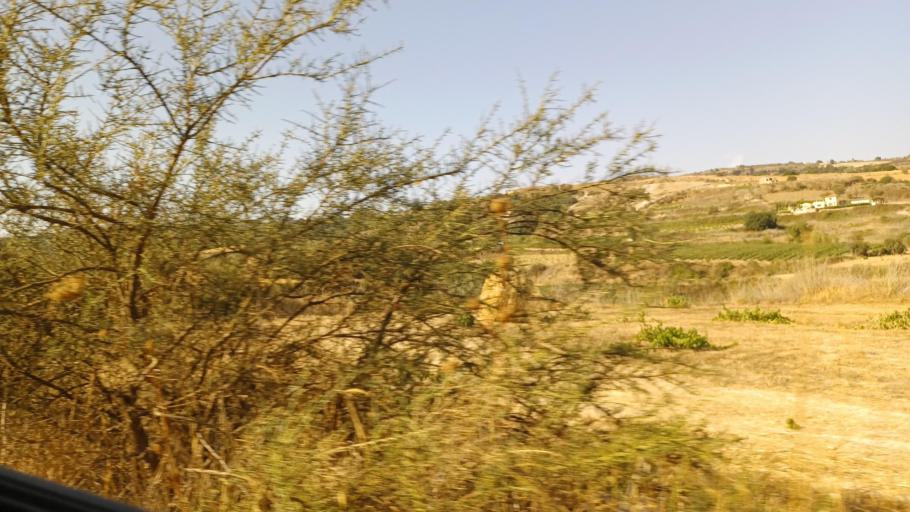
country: CY
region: Pafos
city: Tala
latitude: 34.9077
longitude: 32.4854
